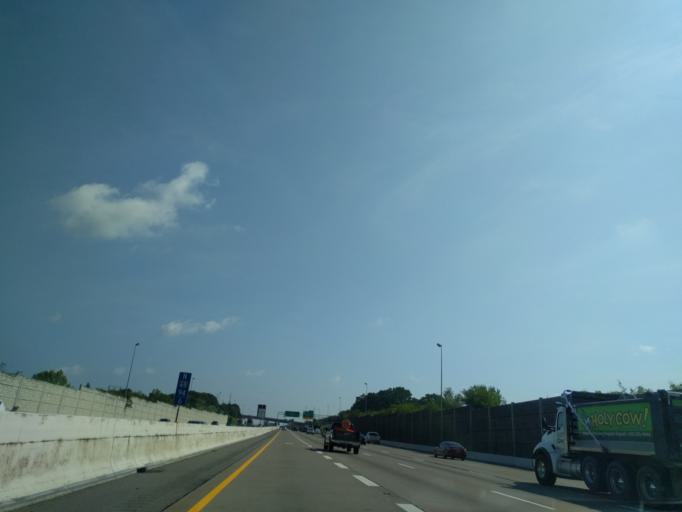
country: US
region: Tennessee
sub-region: Davidson County
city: Goodlettsville
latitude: 36.2936
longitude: -86.7187
